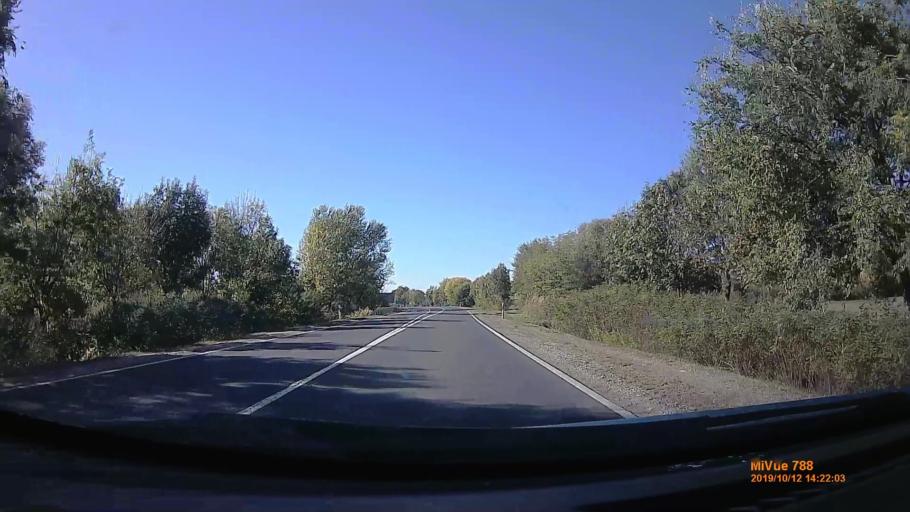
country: HU
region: Hajdu-Bihar
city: Biharkeresztes
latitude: 47.1417
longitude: 21.7223
